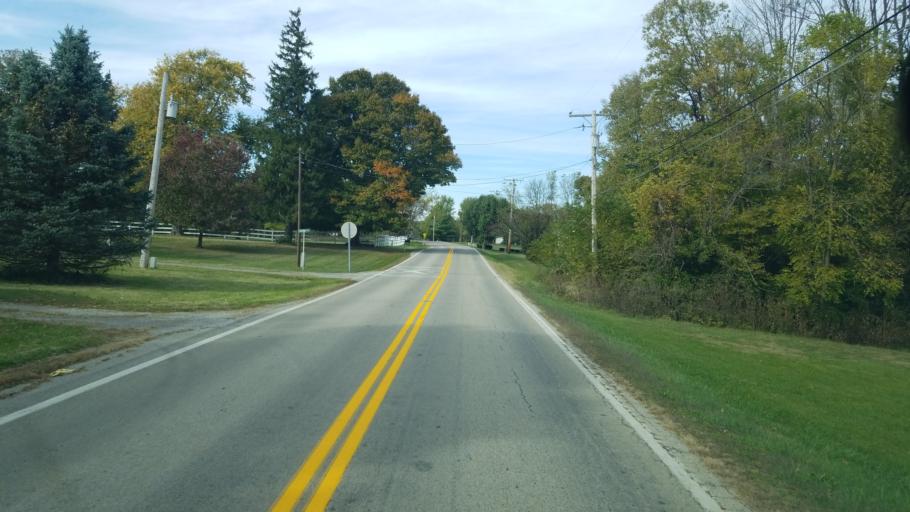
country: US
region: Ohio
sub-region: Highland County
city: Leesburg
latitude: 39.3360
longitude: -83.5931
